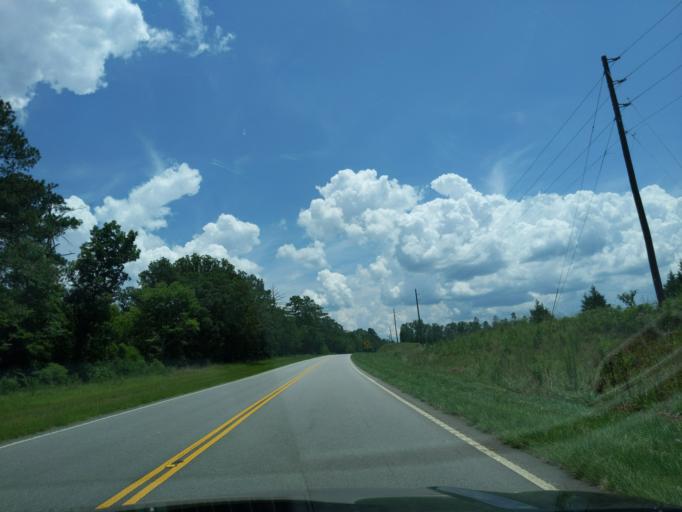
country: US
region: South Carolina
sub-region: Edgefield County
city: Edgefield
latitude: 33.8612
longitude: -81.9851
